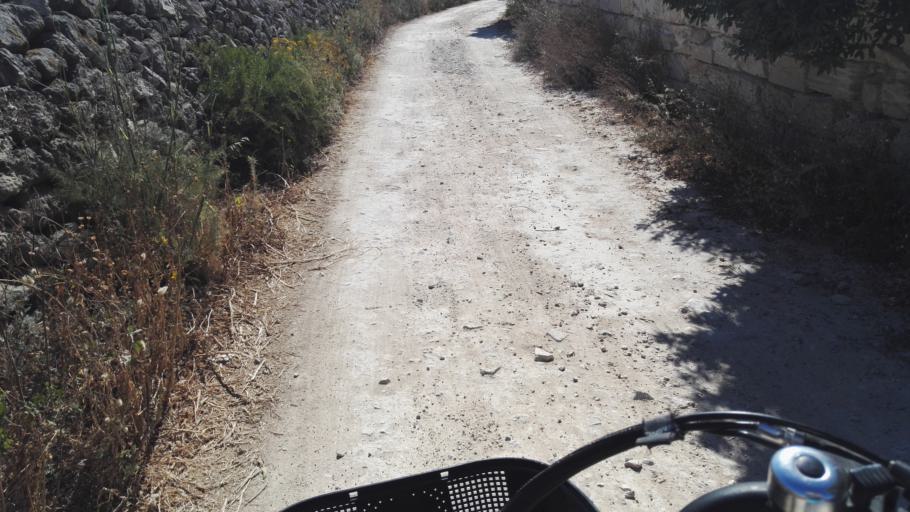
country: IT
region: Sicily
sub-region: Trapani
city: Favignana
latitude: 37.9344
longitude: 12.3359
